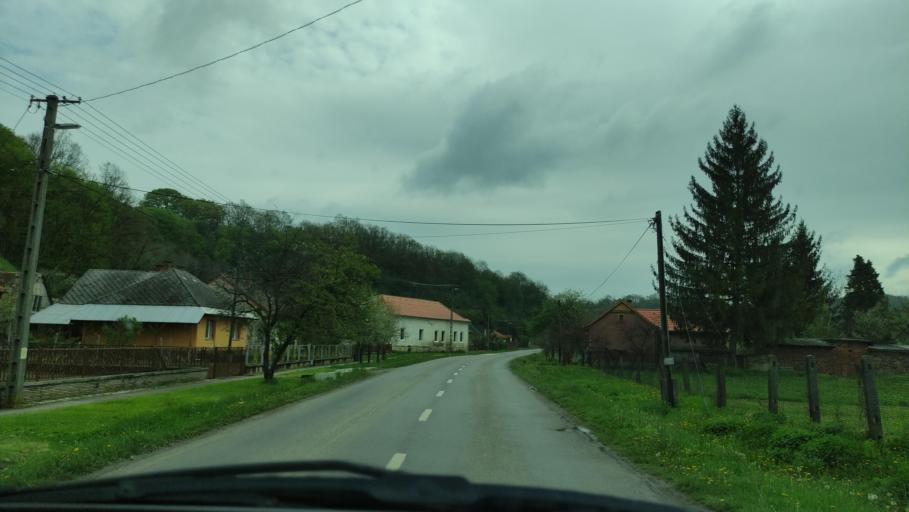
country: HU
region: Baranya
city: Komlo
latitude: 46.2245
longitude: 18.2132
